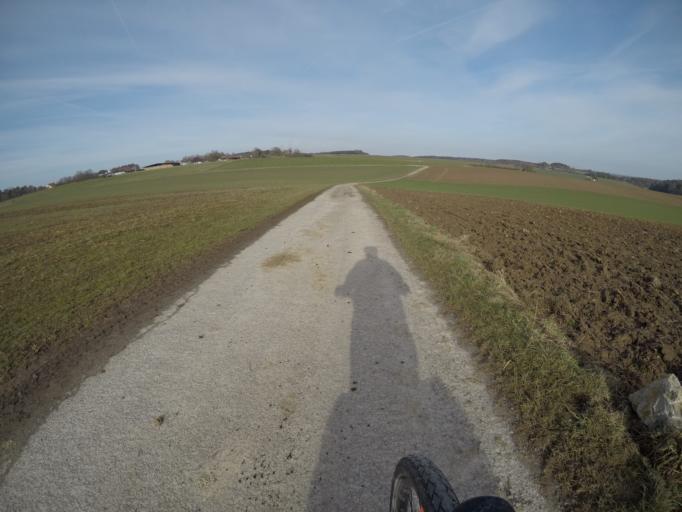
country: DE
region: Baden-Wuerttemberg
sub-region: Karlsruhe Region
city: Ostelsheim
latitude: 48.6985
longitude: 8.8625
